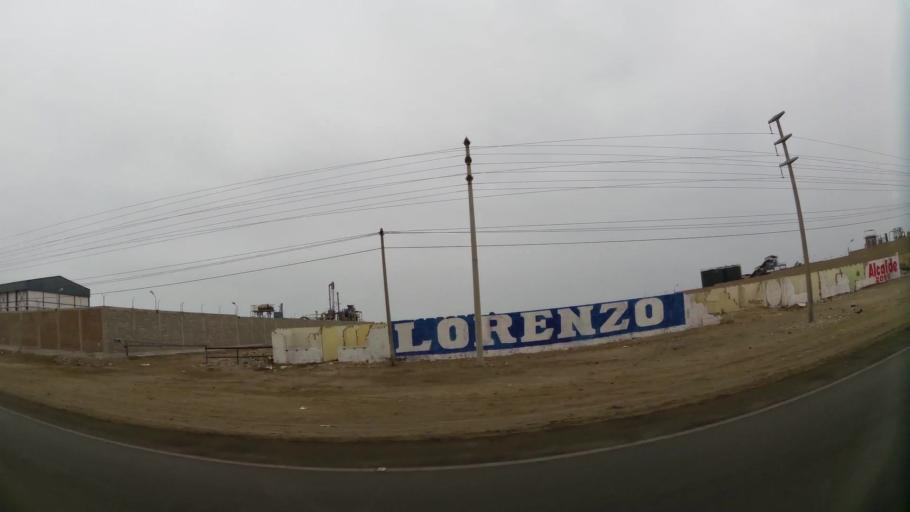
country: PE
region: Ica
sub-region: Provincia de Pisco
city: Pisco
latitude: -13.7857
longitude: -76.2388
